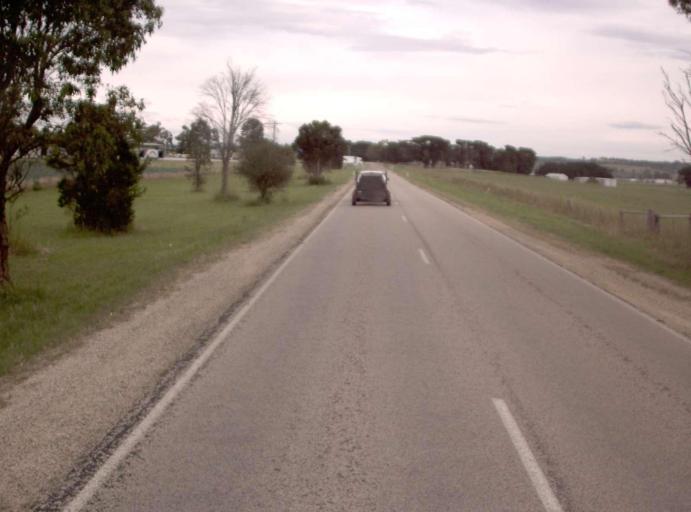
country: AU
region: Victoria
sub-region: East Gippsland
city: Bairnsdale
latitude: -37.8135
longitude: 147.4890
